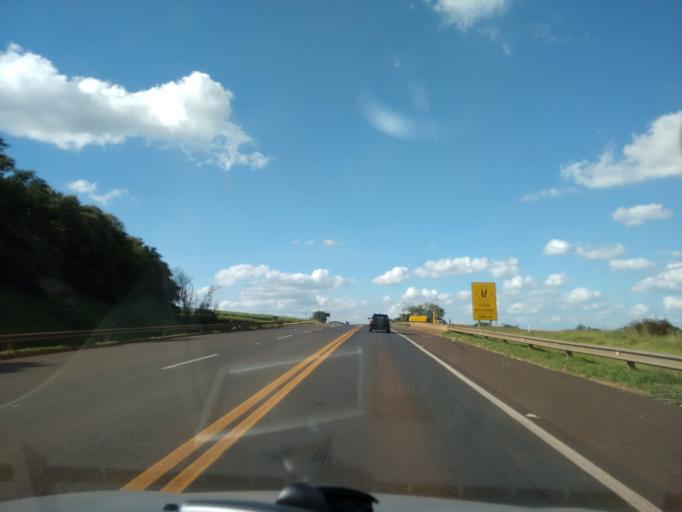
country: BR
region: Sao Paulo
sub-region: Americo Brasiliense
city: Americo Brasiliense
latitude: -21.7563
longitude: -48.0708
